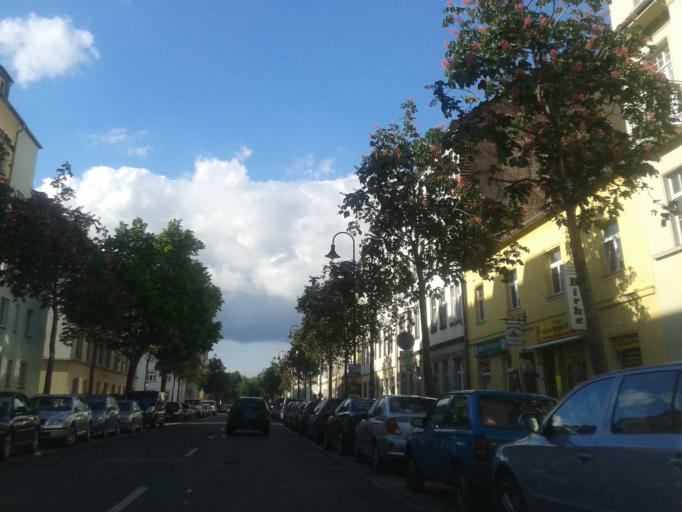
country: DE
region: Saxony
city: Dresden
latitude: 51.0816
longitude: 13.7203
